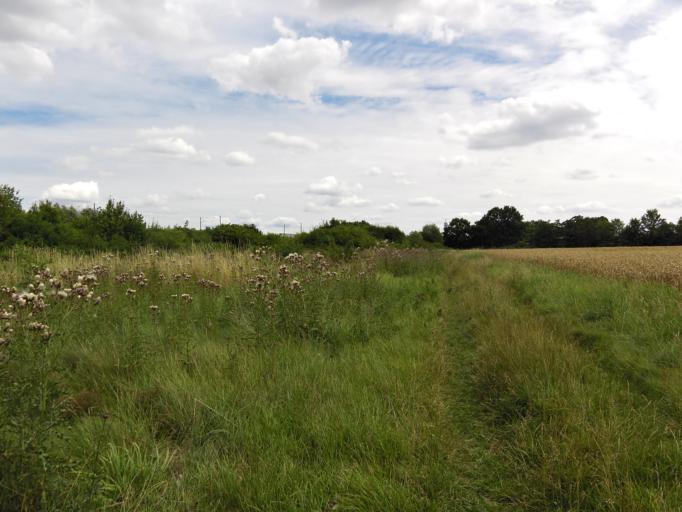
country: DE
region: Saxony
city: Rackwitz
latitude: 51.4042
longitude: 12.3822
